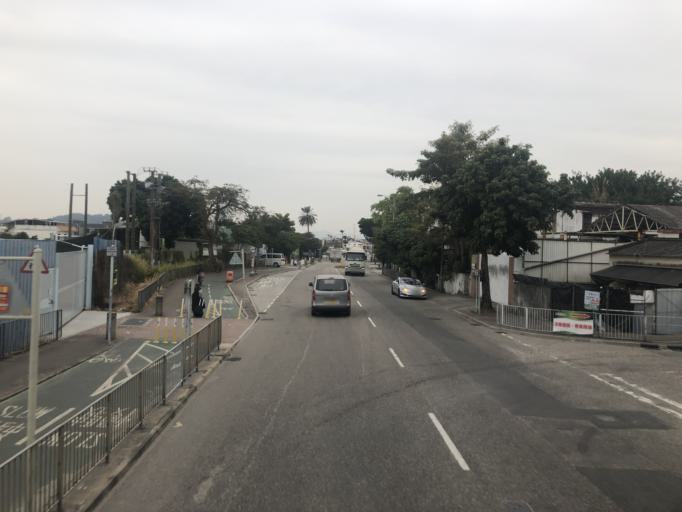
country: HK
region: Yuen Long
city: Yuen Long Kau Hui
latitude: 22.4324
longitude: 113.9927
